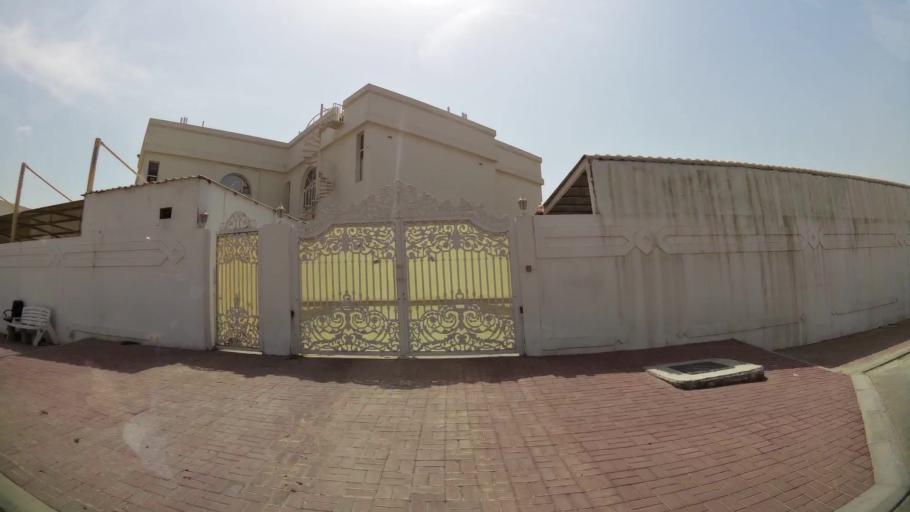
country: AE
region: Ash Shariqah
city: Sharjah
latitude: 25.2326
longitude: 55.4481
